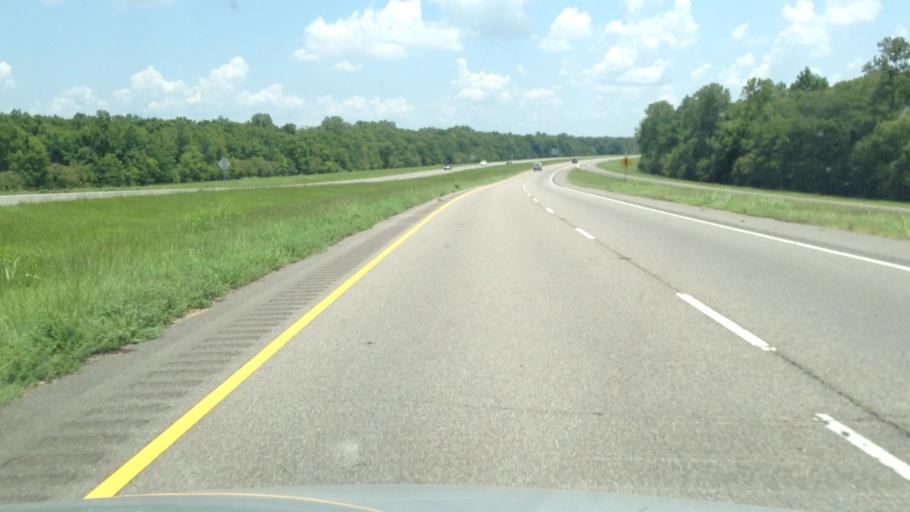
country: US
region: Louisiana
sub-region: Avoyelles Parish
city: Bunkie
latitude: 30.9867
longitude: -92.3072
